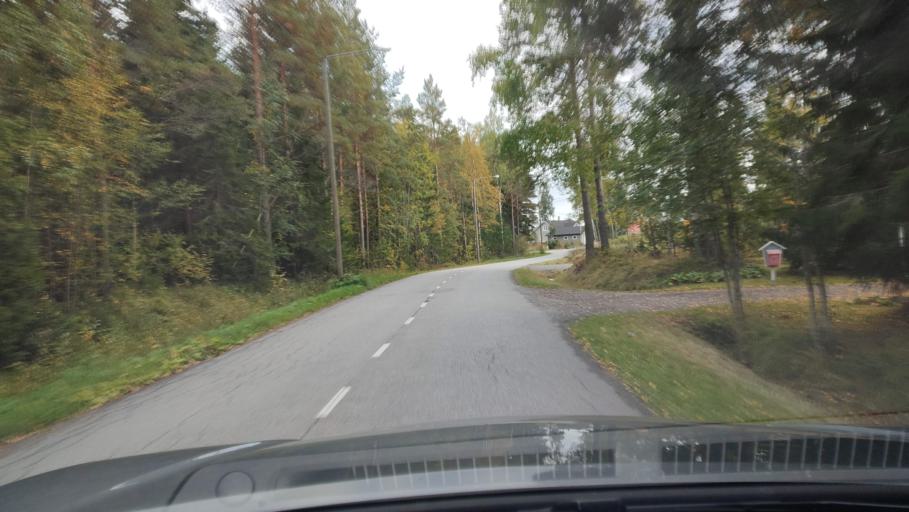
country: FI
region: Ostrobothnia
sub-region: Sydosterbotten
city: Kristinestad
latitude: 62.2579
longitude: 21.3839
